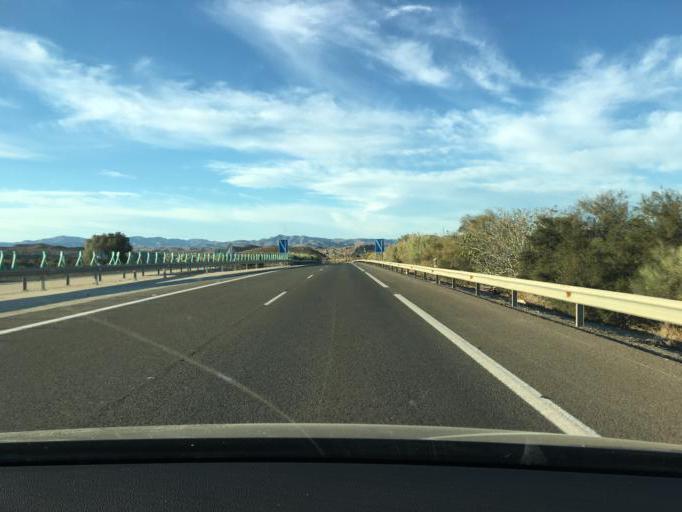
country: ES
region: Andalusia
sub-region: Provincia de Almeria
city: Sorbas
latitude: 37.0784
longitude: -2.0560
